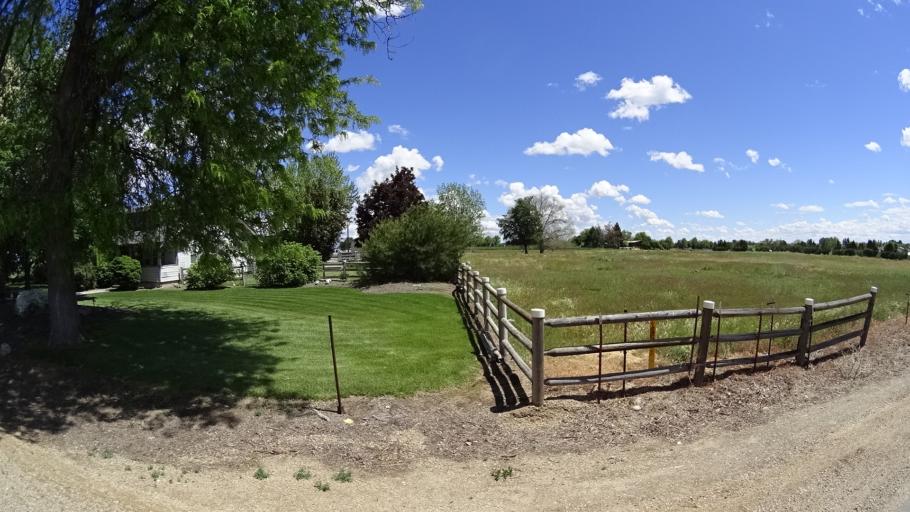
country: US
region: Idaho
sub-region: Ada County
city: Kuna
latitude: 43.5571
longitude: -116.4338
